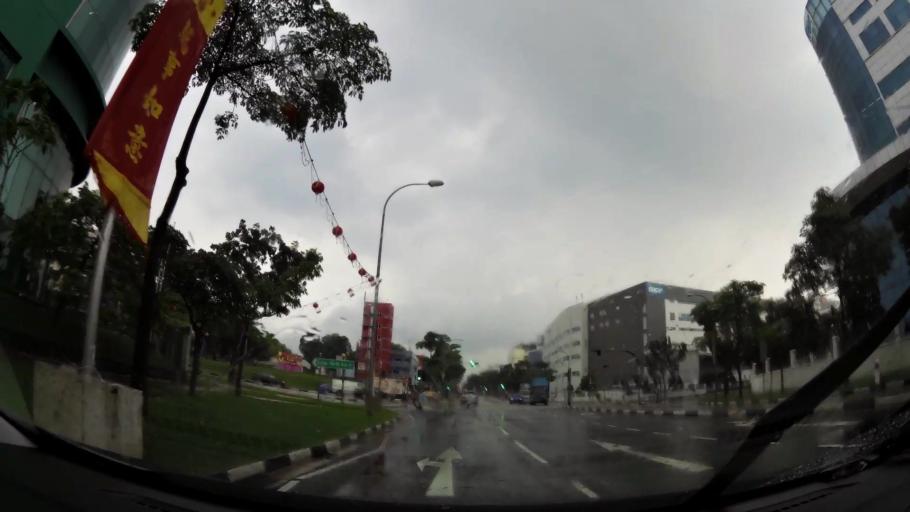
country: SG
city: Singapore
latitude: 1.3343
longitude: 103.9503
